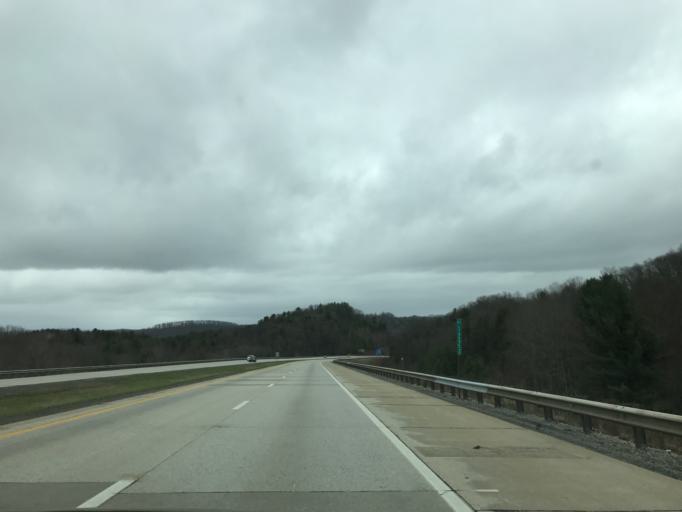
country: US
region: West Virginia
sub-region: Raleigh County
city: Beaver
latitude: 37.7454
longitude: -81.1655
